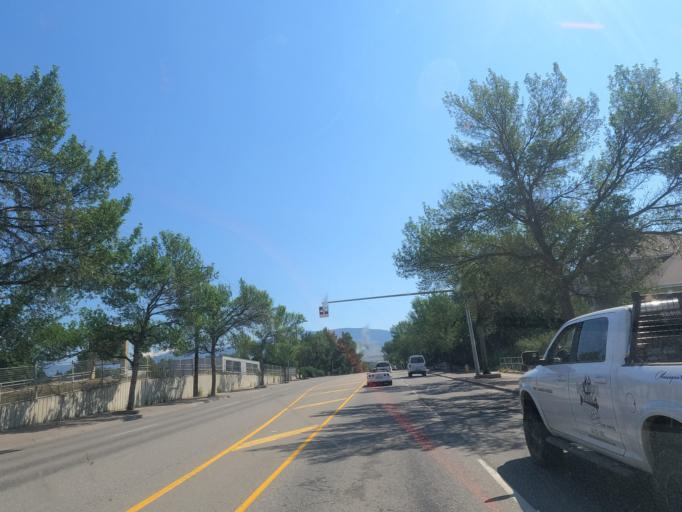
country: CA
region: British Columbia
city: Kelowna
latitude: 49.8890
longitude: -119.4052
